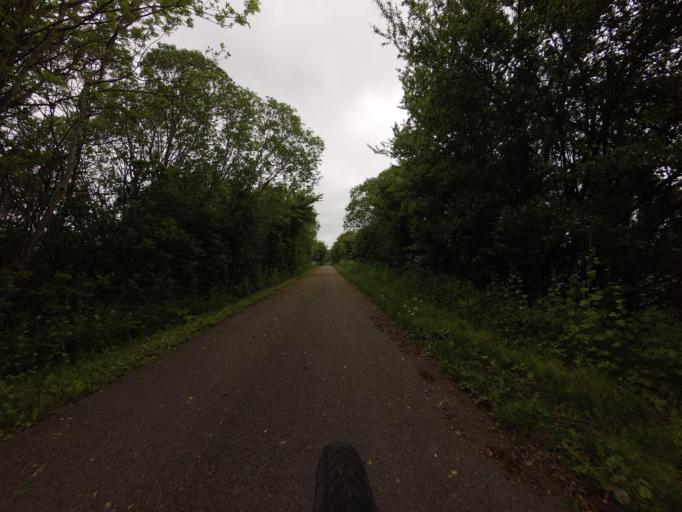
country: DK
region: Zealand
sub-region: Naestved Kommune
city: Fuglebjerg
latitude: 55.2835
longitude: 11.4249
